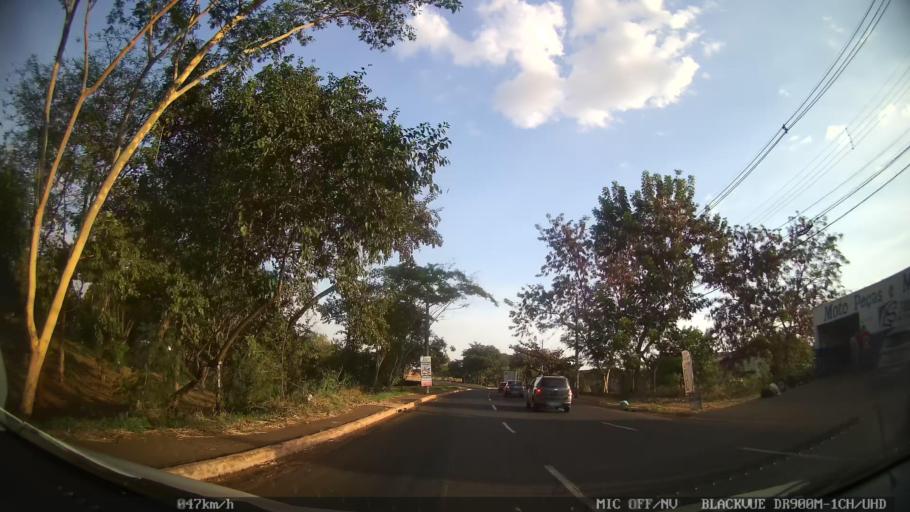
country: BR
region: Sao Paulo
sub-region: Ribeirao Preto
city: Ribeirao Preto
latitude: -21.1445
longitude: -47.8040
